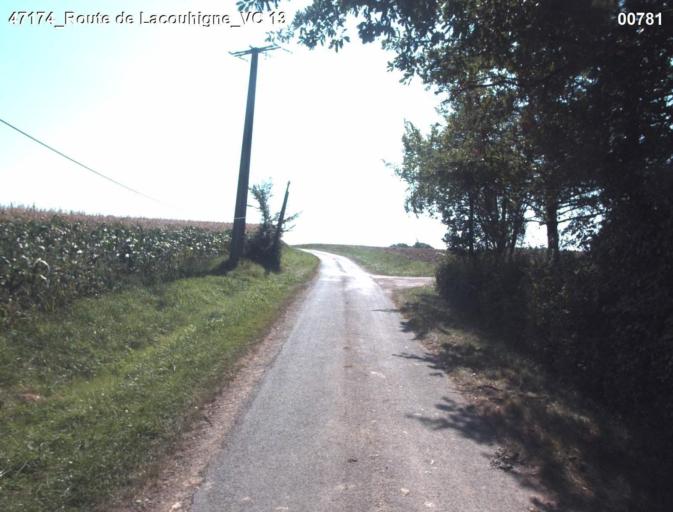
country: FR
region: Midi-Pyrenees
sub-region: Departement du Gers
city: Condom
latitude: 44.0208
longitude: 0.3835
